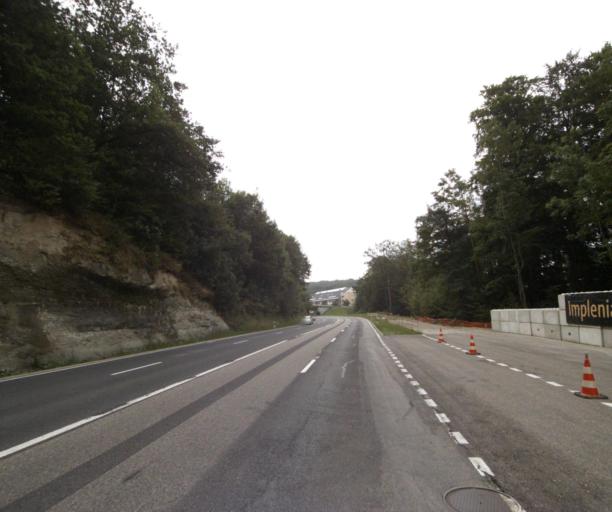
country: CH
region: Vaud
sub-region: Lausanne District
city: Epalinges
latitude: 46.5497
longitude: 6.6706
